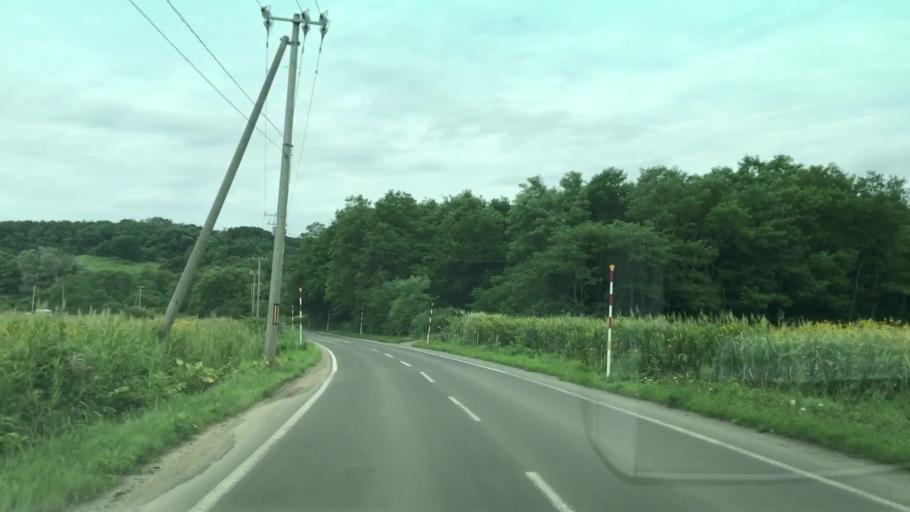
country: JP
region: Hokkaido
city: Iwanai
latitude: 43.0371
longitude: 140.5469
